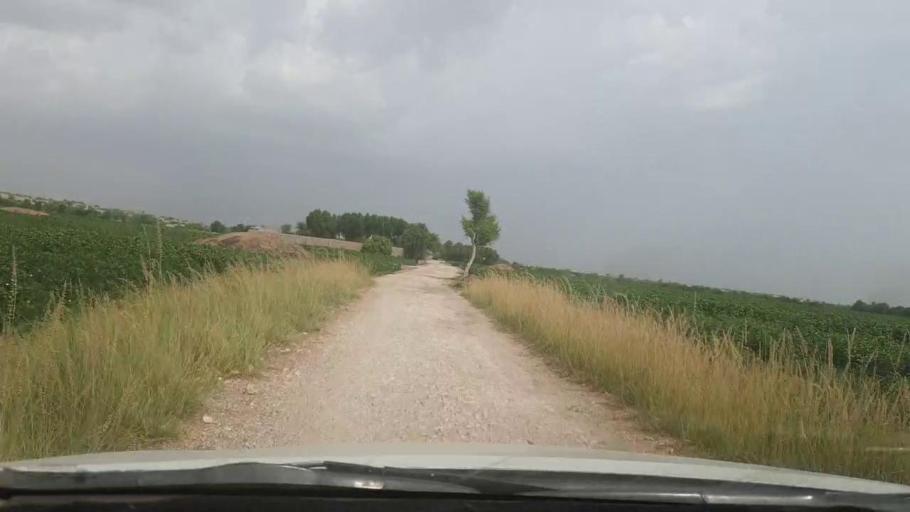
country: PK
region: Sindh
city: Kot Diji
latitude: 27.3370
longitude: 69.0356
